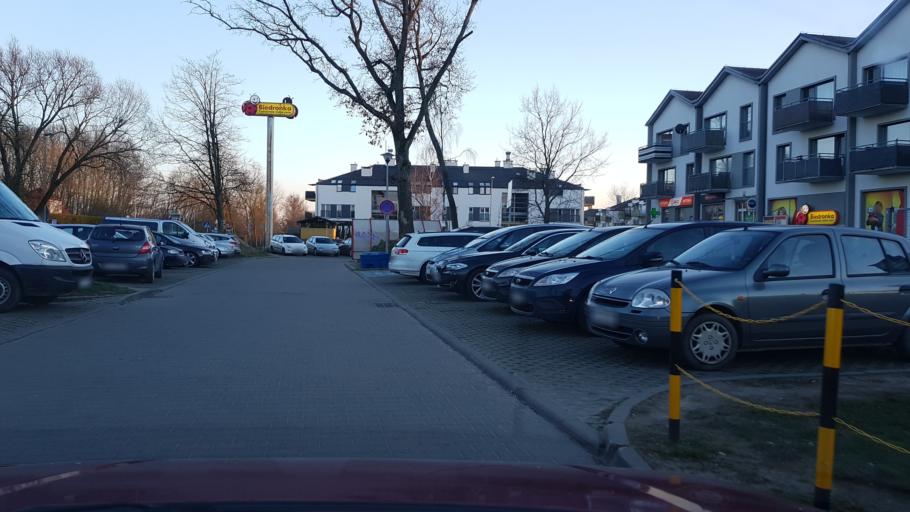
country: PL
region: West Pomeranian Voivodeship
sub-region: Szczecin
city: Szczecin
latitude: 53.4822
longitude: 14.5433
